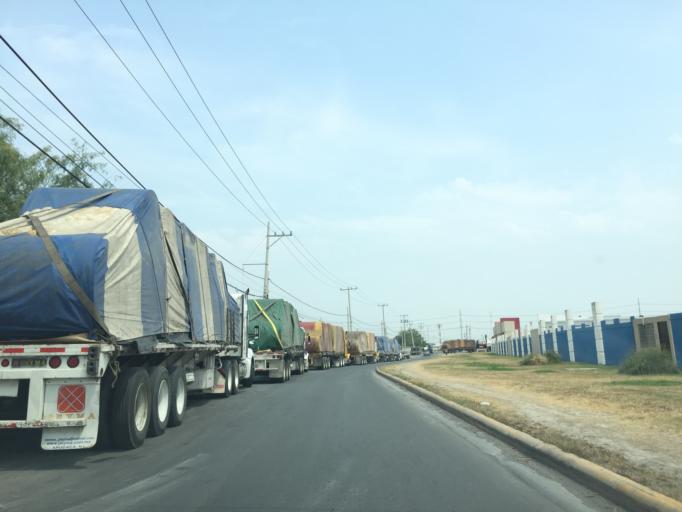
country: MX
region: Nuevo Leon
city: Apodaca
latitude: 25.7629
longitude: -100.1972
